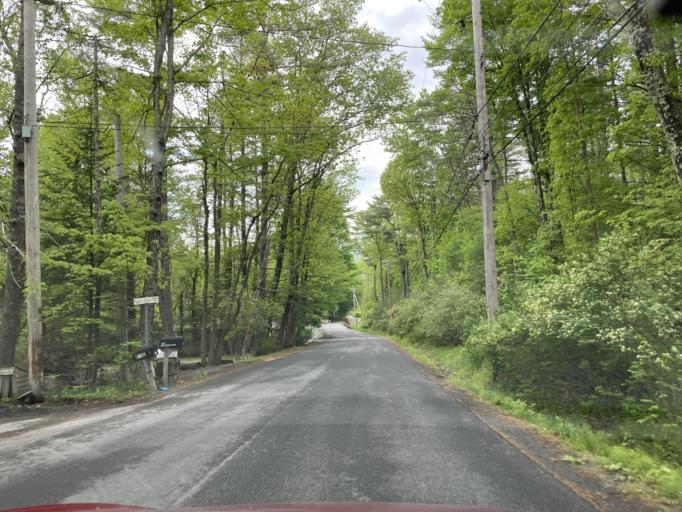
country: US
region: New York
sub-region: Ulster County
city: Woodstock
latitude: 42.0339
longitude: -74.1469
